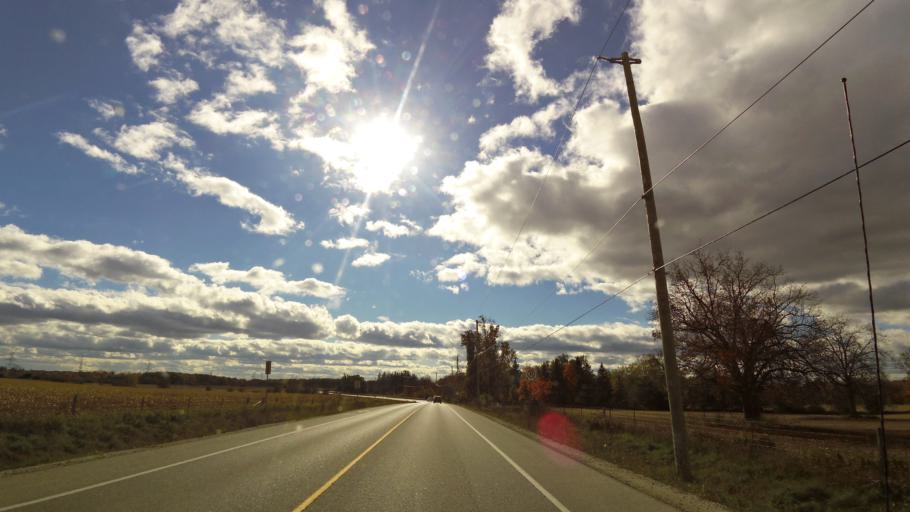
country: CA
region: Ontario
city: Oakville
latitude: 43.5052
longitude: -79.7659
